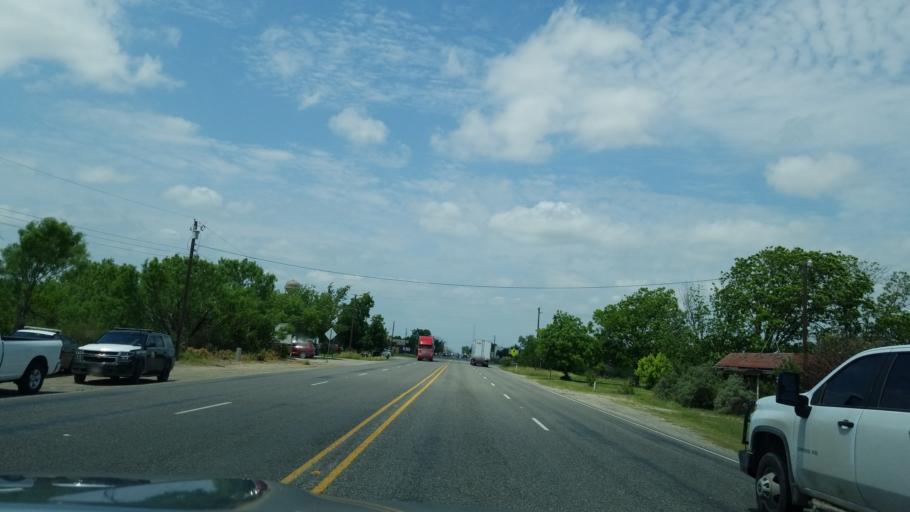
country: US
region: Texas
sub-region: Zavala County
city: La Pryor
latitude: 28.9455
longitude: -99.8374
